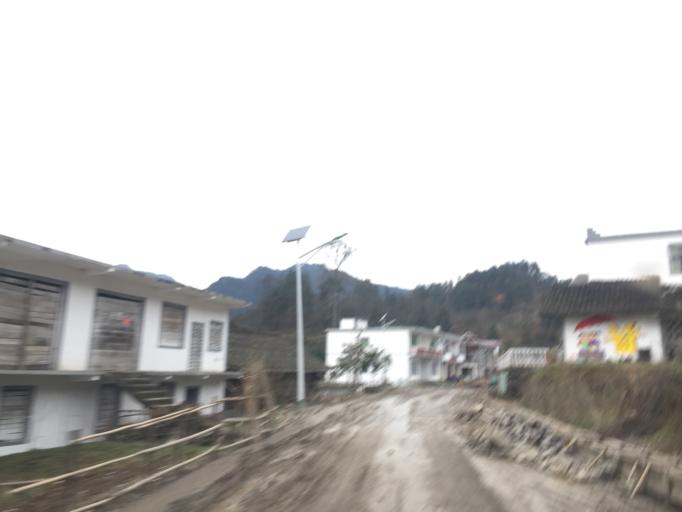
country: CN
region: Guizhou Sheng
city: Changfeng
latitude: 28.4494
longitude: 108.0761
